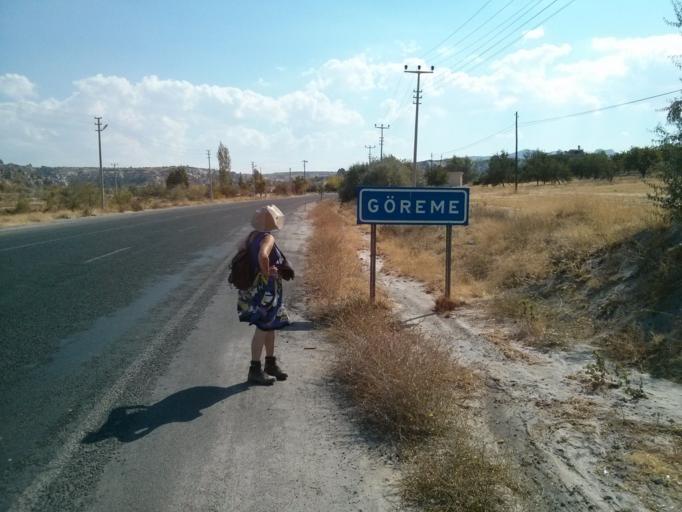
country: TR
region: Nevsehir
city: Goereme
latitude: 38.6541
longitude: 34.8364
